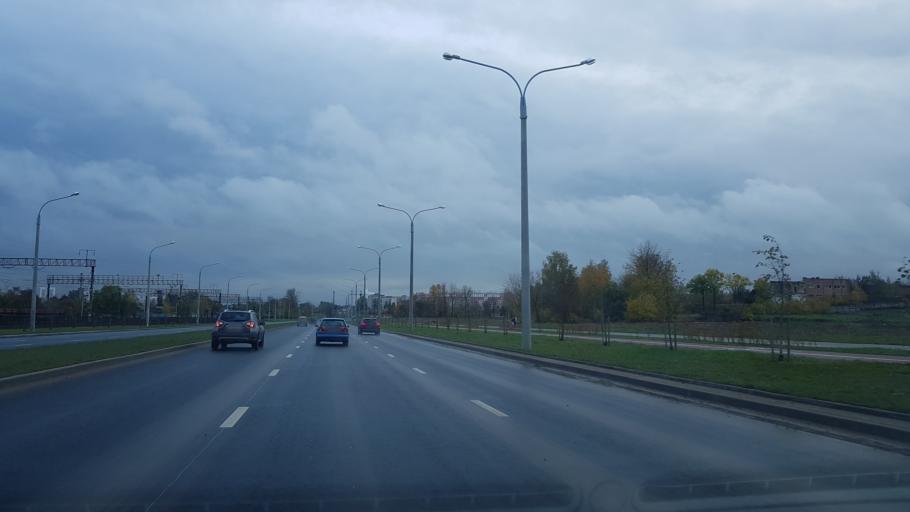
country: BY
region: Minsk
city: Minsk
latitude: 53.8640
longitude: 27.5593
